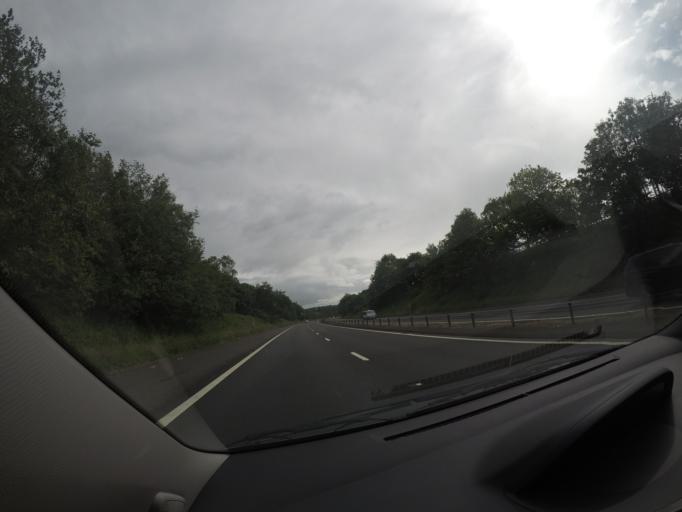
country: GB
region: Scotland
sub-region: Falkirk
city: Dunipace
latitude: 56.0416
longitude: -3.9175
